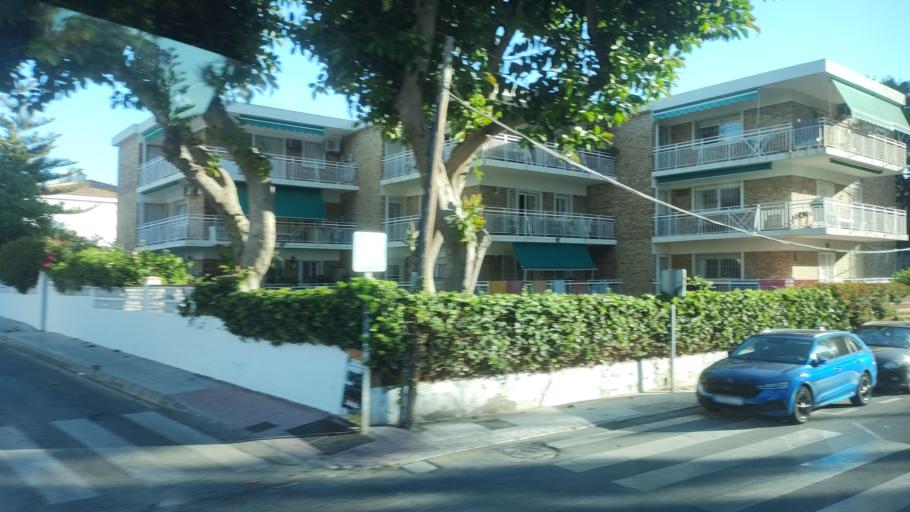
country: ES
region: Andalusia
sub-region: Provincia de Malaga
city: Torremolinos
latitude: 36.6303
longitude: -4.4944
